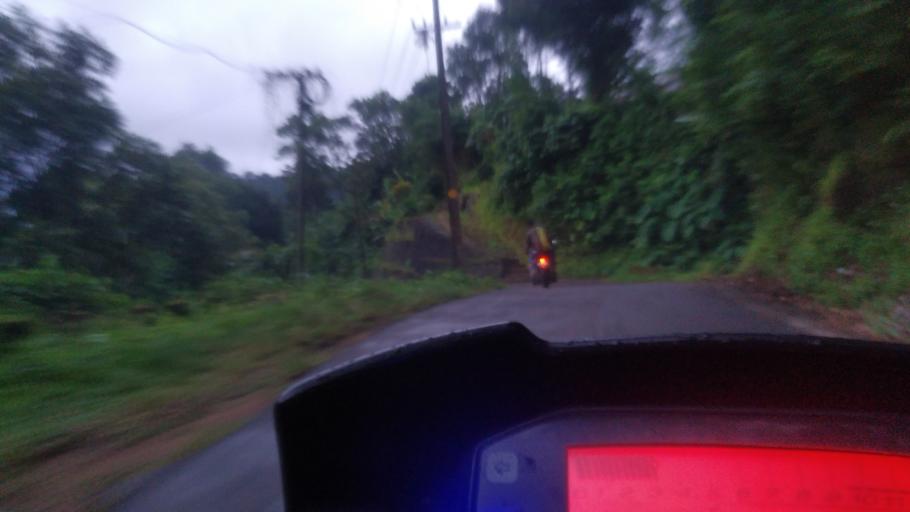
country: IN
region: Kerala
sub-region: Kottayam
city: Erattupetta
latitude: 9.5518
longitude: 76.9713
